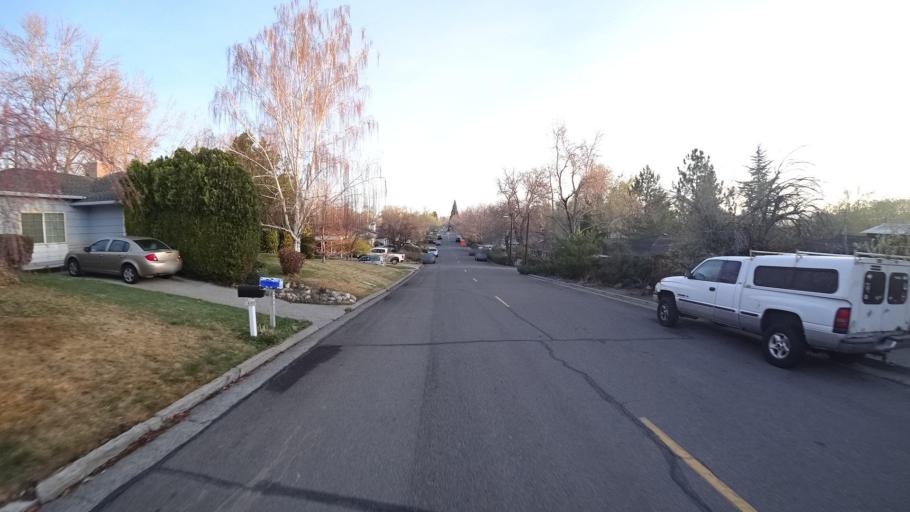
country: US
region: Nevada
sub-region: Washoe County
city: Reno
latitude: 39.5074
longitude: -119.8153
